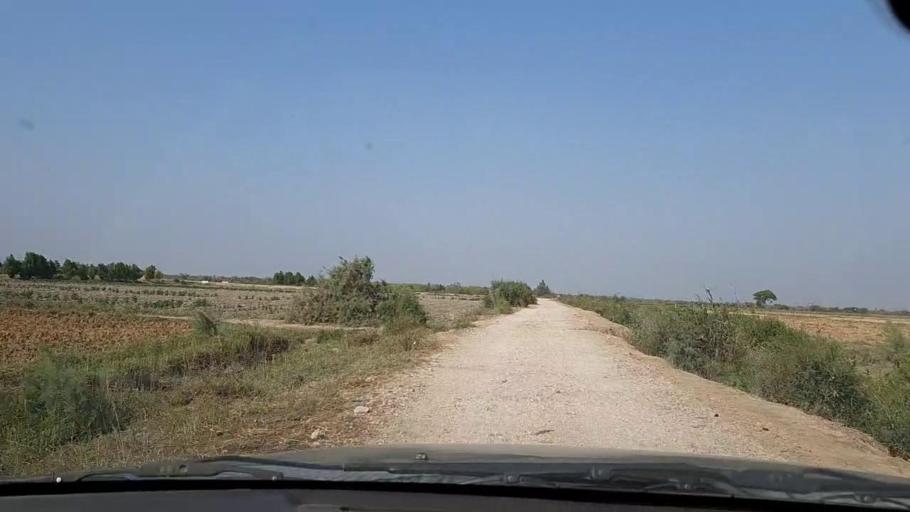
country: PK
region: Sindh
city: Mirpur Sakro
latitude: 24.3752
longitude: 67.6829
